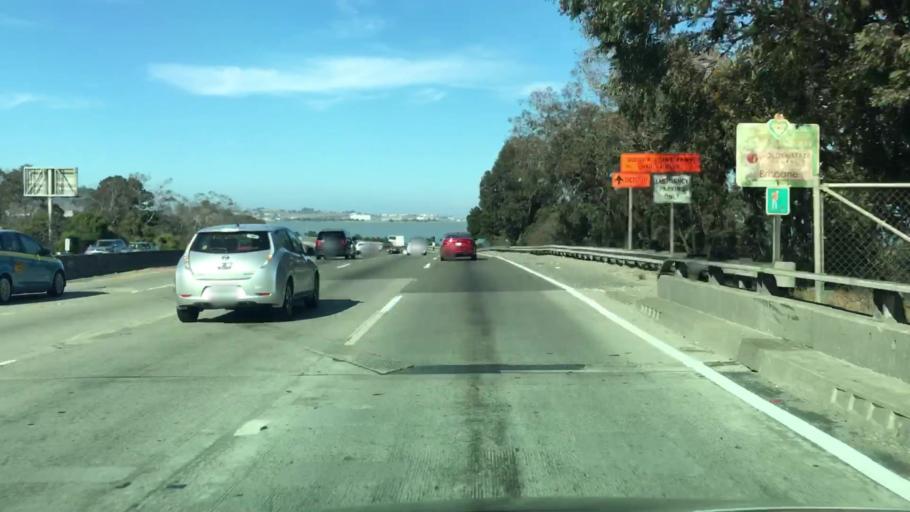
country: US
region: California
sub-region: San Mateo County
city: Brisbane
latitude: 37.6749
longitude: -122.3891
